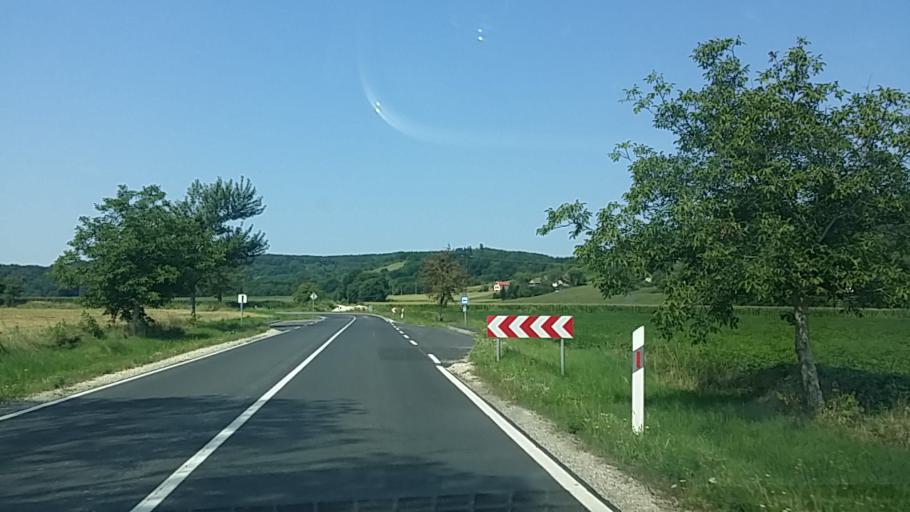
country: HU
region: Zala
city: Lenti
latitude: 46.5706
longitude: 16.5567
